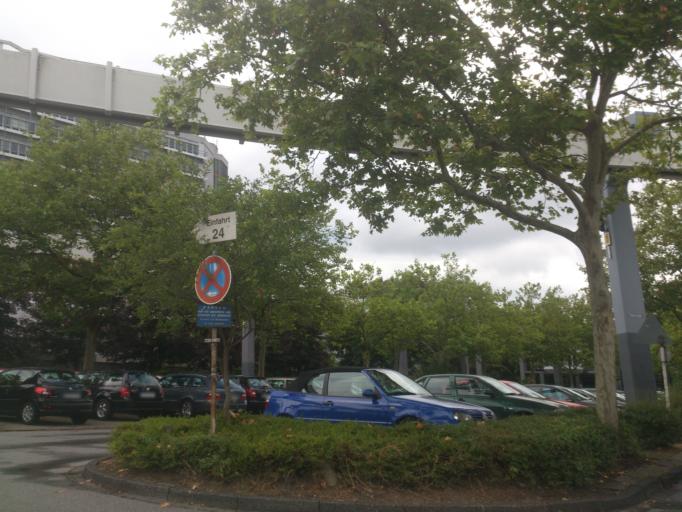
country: DE
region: North Rhine-Westphalia
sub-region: Regierungsbezirk Arnsberg
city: Dortmund
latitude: 51.4918
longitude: 7.4166
